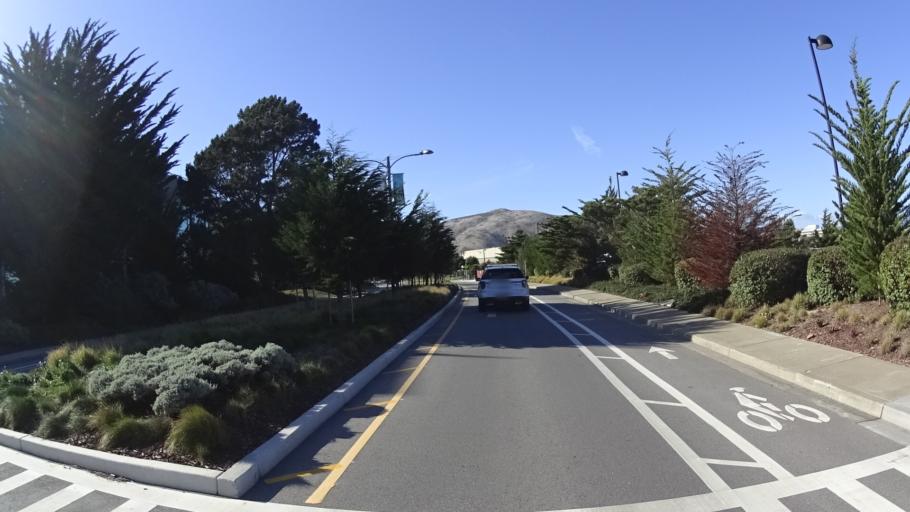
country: US
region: California
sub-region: San Mateo County
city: South San Francisco
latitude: 37.6581
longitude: -122.3791
